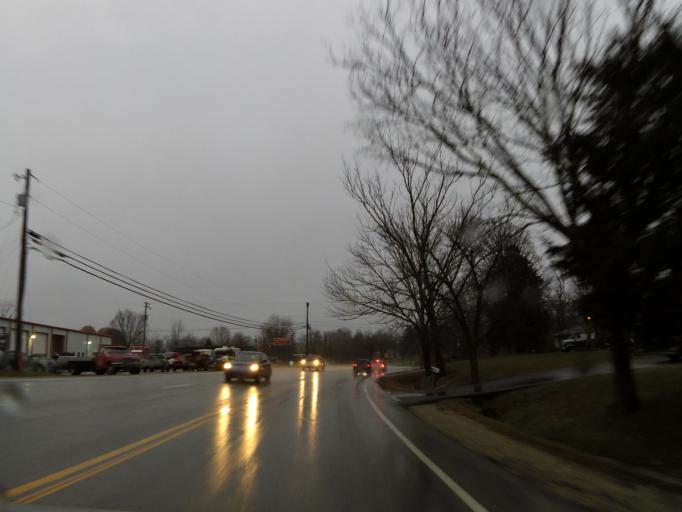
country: US
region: Kentucky
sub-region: Rockcastle County
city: Mount Vernon
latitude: 37.3476
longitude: -84.3173
